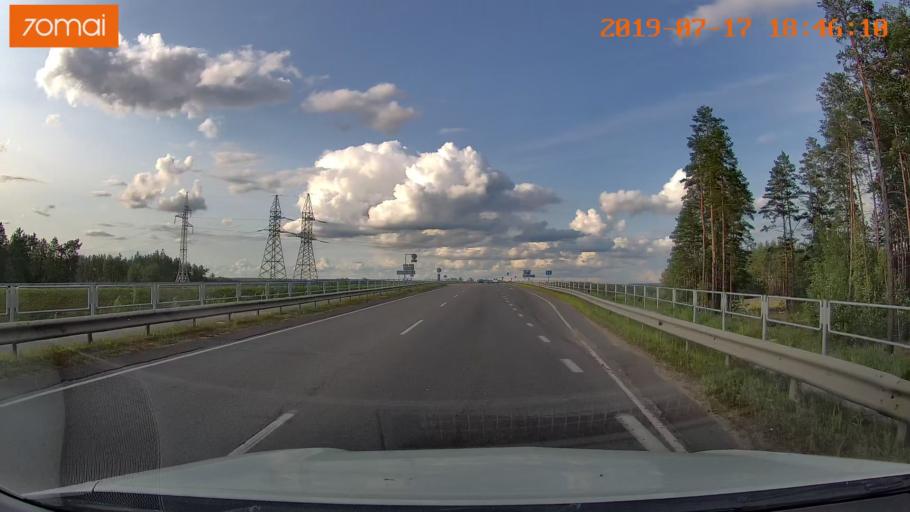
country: BY
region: Mogilev
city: Asipovichy
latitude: 53.3331
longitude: 28.6629
